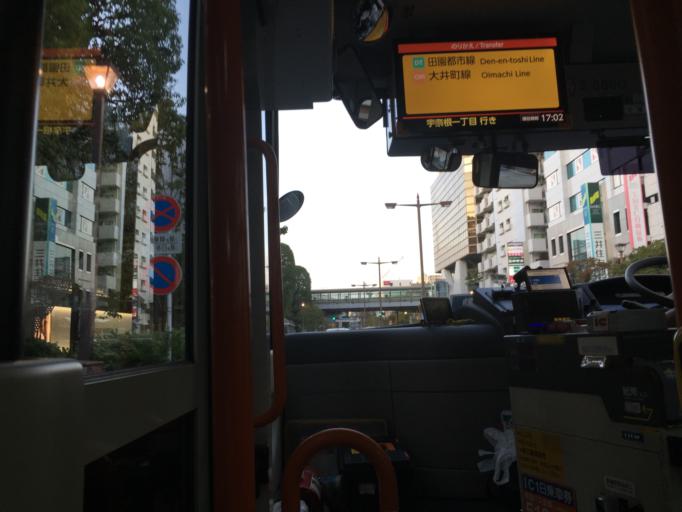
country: JP
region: Tokyo
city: Chofugaoka
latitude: 35.6133
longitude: 139.6270
